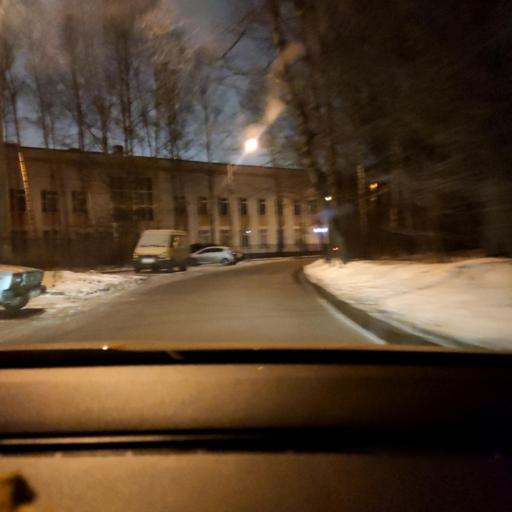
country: RU
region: Moscow
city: Metrogorodok
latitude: 55.8279
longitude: 37.7536
